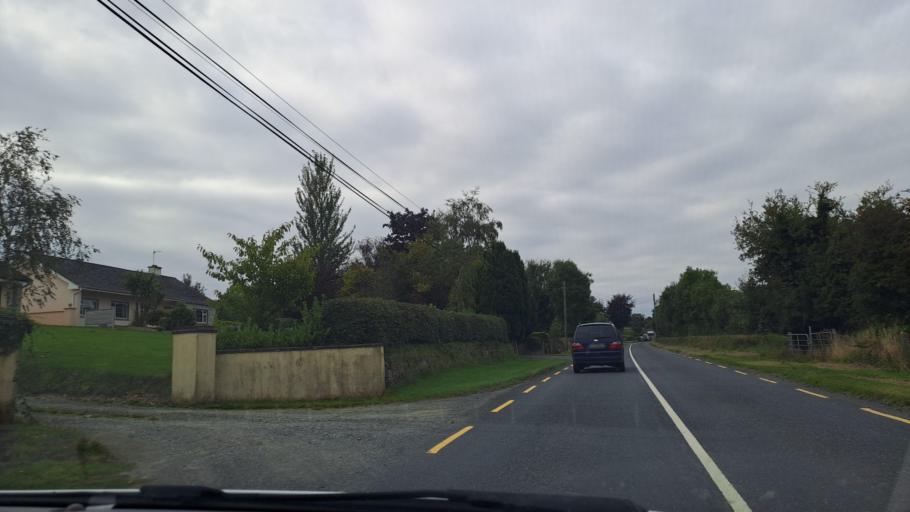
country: IE
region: Ulster
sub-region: County Monaghan
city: Carrickmacross
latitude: 54.0033
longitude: -6.7418
